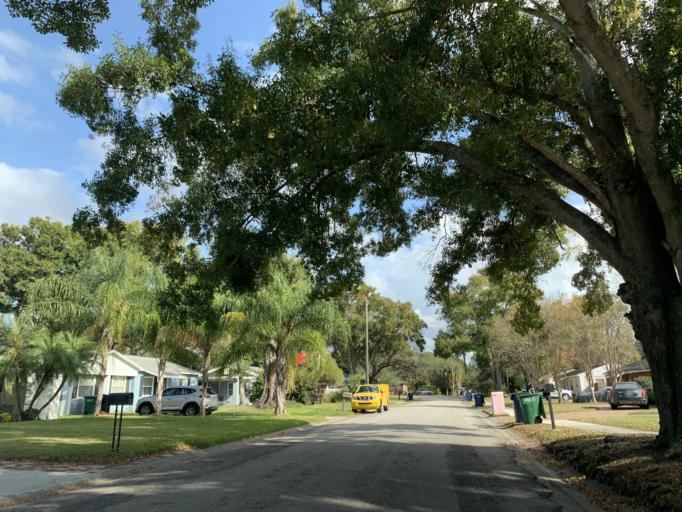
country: US
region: Florida
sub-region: Hillsborough County
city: Tampa
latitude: 27.9079
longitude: -82.5135
